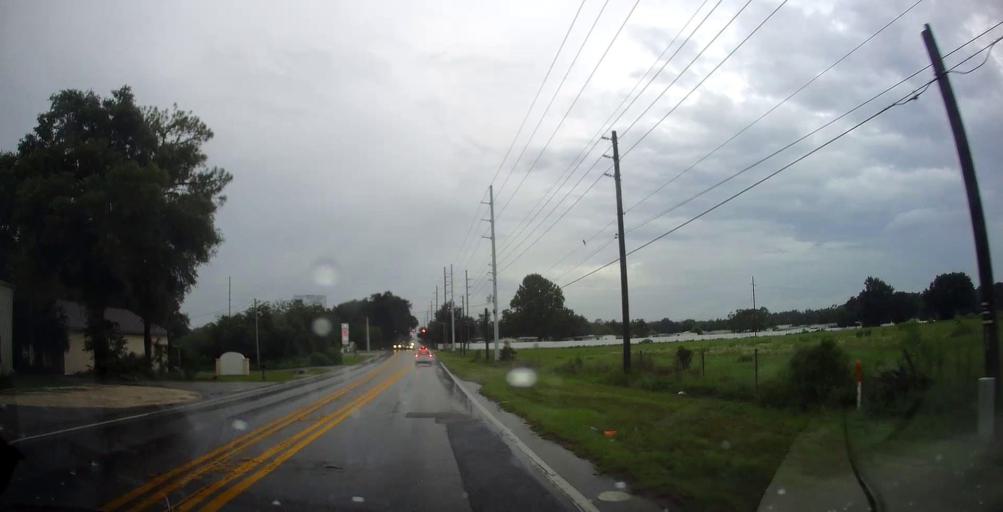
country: US
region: Florida
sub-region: Marion County
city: Ocala
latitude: 29.2246
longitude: -82.0869
